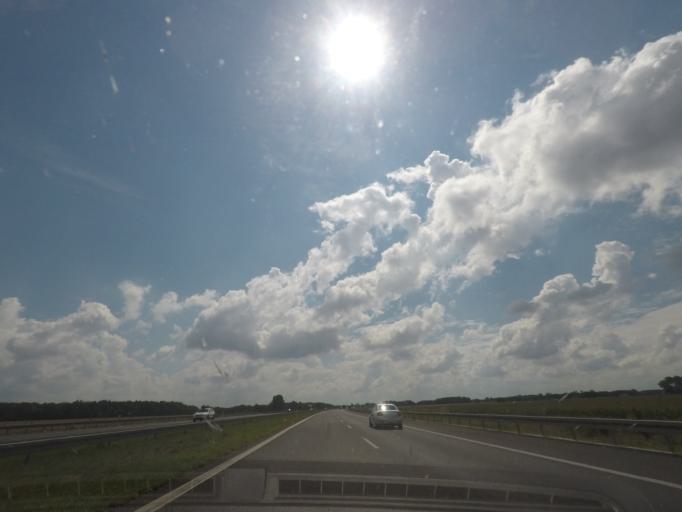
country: PL
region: Lodz Voivodeship
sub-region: Powiat zgierski
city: Strykow
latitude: 51.9527
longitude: 19.6012
